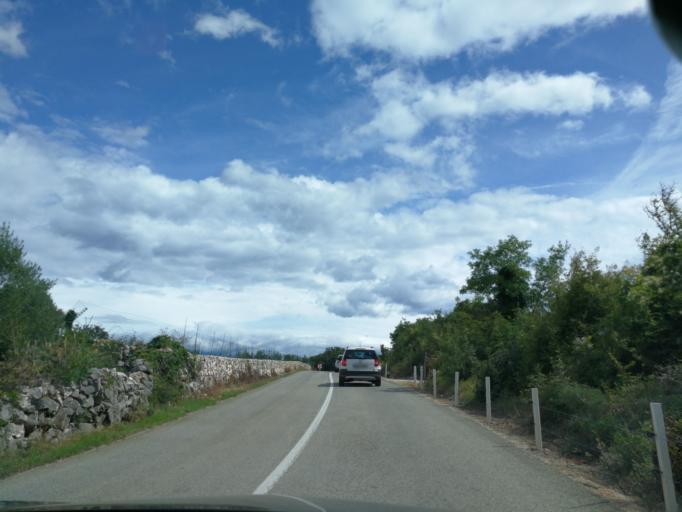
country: HR
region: Primorsko-Goranska
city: Punat
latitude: 45.0783
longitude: 14.6573
